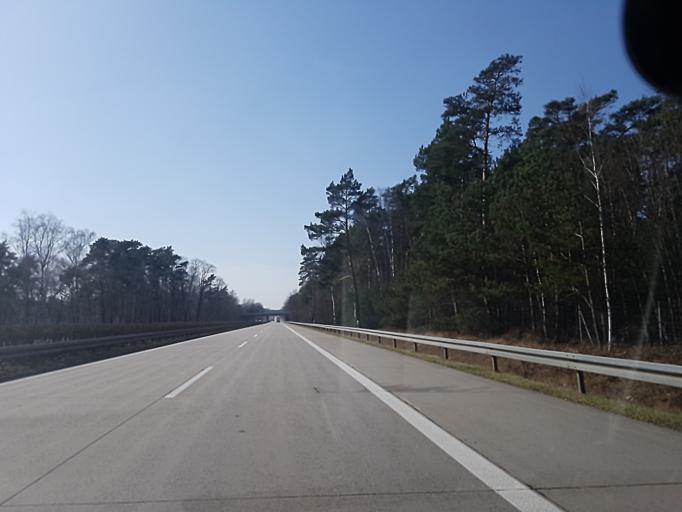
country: DE
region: Brandenburg
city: Heinersbruck
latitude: 51.7116
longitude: 14.5001
